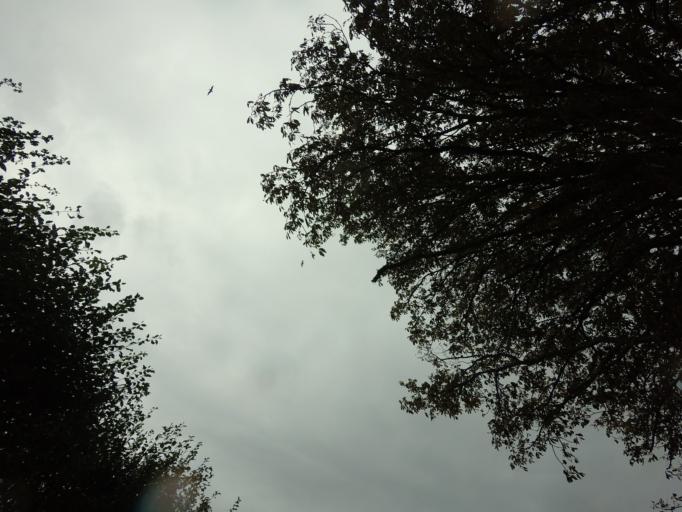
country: GB
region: England
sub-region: Cambridgeshire
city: Duxford
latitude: 52.0547
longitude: 0.1284
